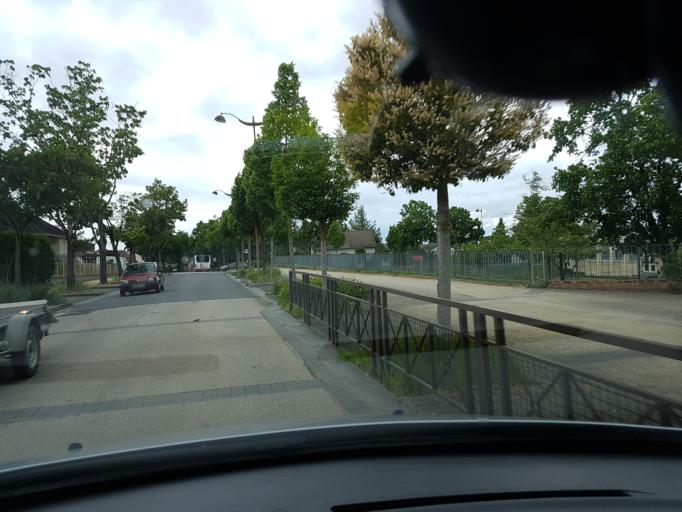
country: FR
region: Centre
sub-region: Departement du Cher
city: Bourges
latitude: 47.1098
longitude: 2.4172
